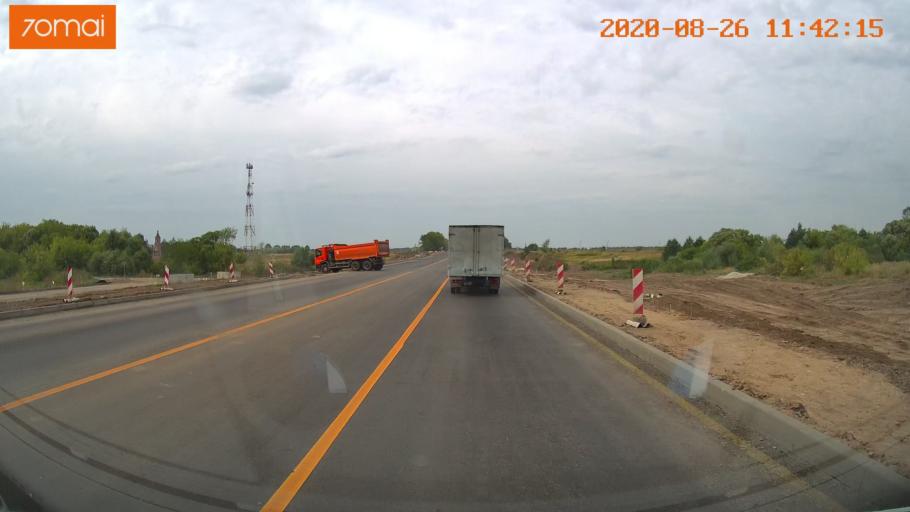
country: RU
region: Rjazan
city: Shilovo
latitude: 54.2973
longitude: 40.6972
